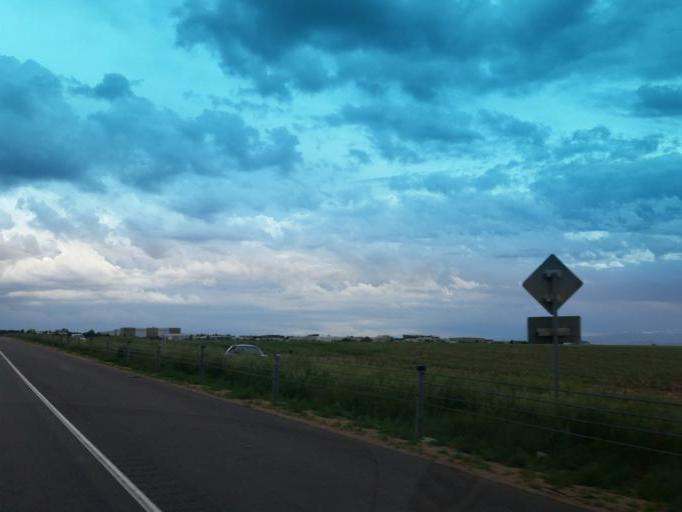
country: US
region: Colorado
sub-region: Weld County
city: Windsor
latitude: 40.4640
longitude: -104.9922
